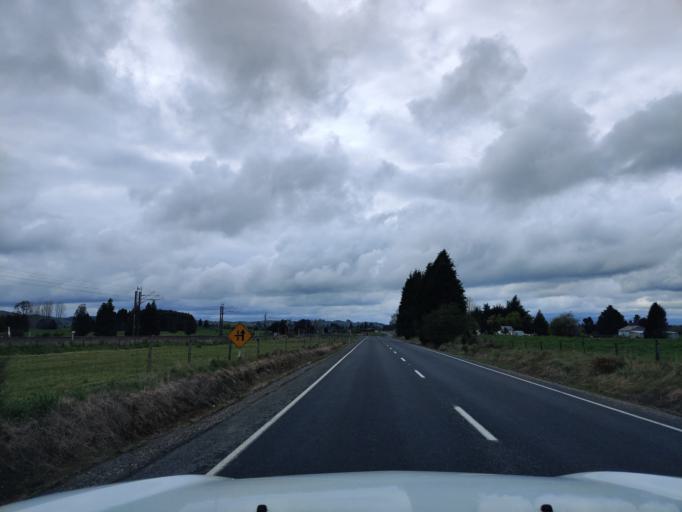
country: NZ
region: Waikato
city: Turangi
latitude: -39.0151
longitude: 175.3784
